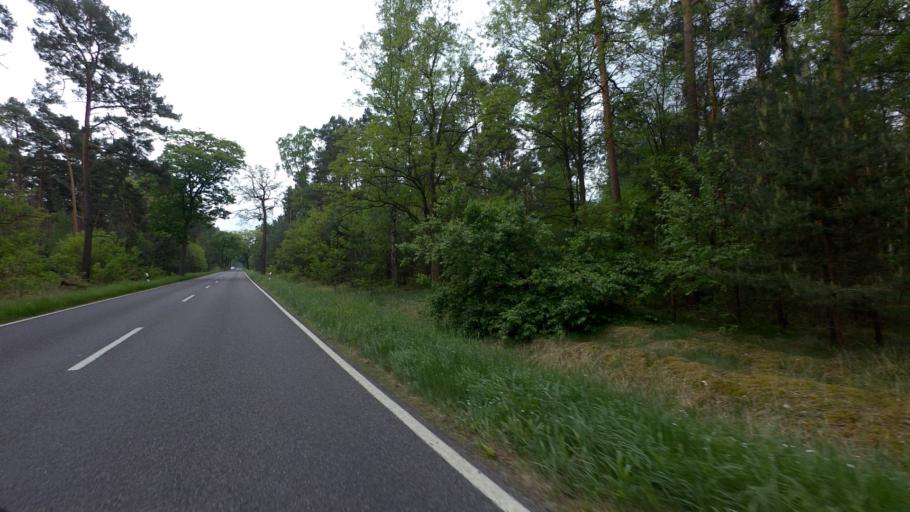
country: DE
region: Brandenburg
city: Halbe
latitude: 52.1288
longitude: 13.7539
